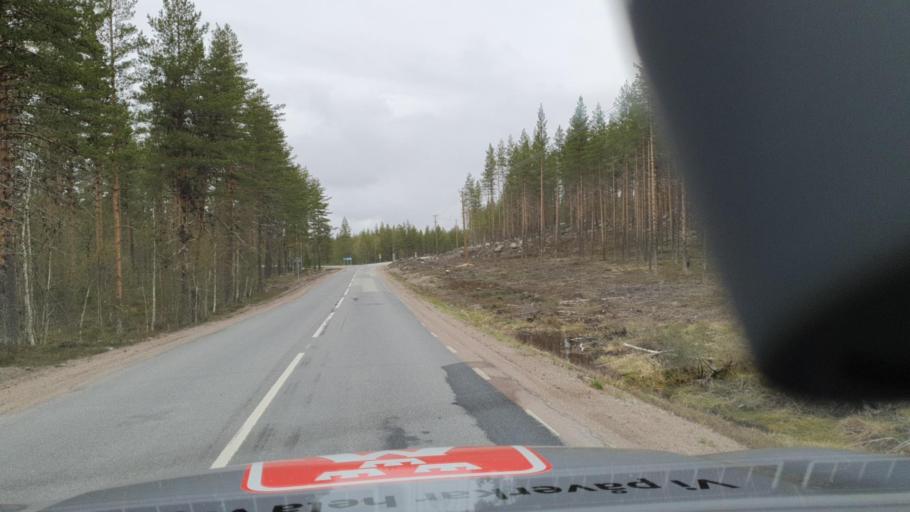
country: SE
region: Vaesternorrland
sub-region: Solleftea Kommun
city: Solleftea
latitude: 63.6390
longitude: 17.4173
